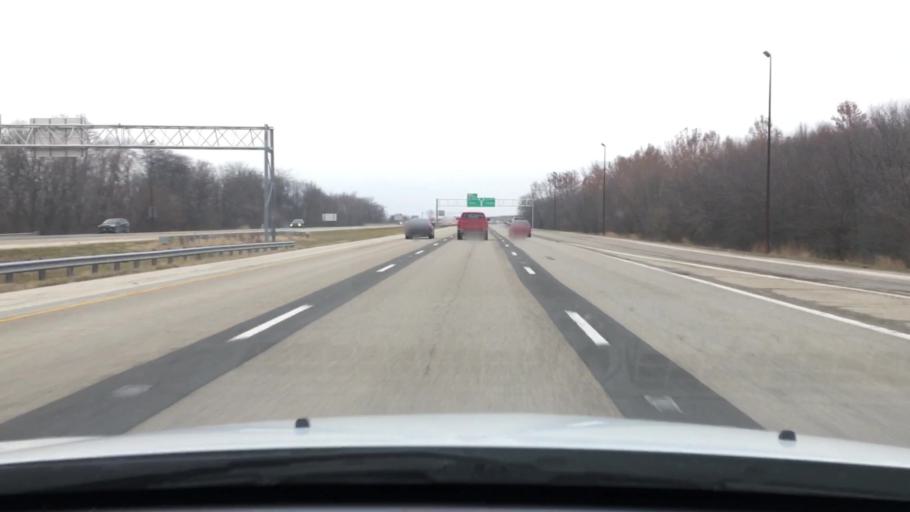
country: US
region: Illinois
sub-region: Logan County
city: Lincoln
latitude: 40.1648
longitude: -89.4176
